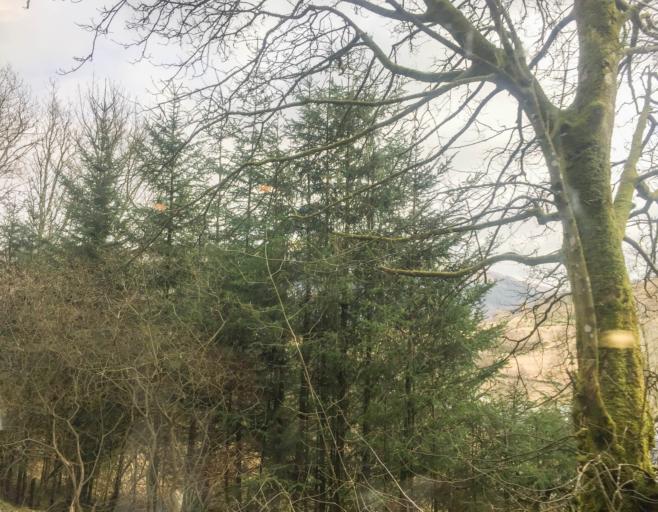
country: GB
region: Scotland
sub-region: Argyll and Bute
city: Garelochhead
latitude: 56.2040
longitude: -4.7211
